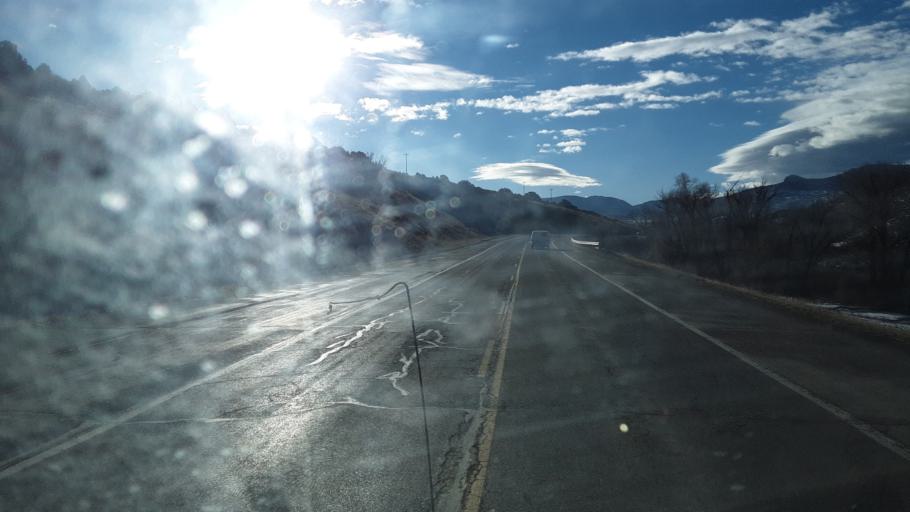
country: US
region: Colorado
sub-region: Montrose County
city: Montrose
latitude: 38.4264
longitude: -107.5351
